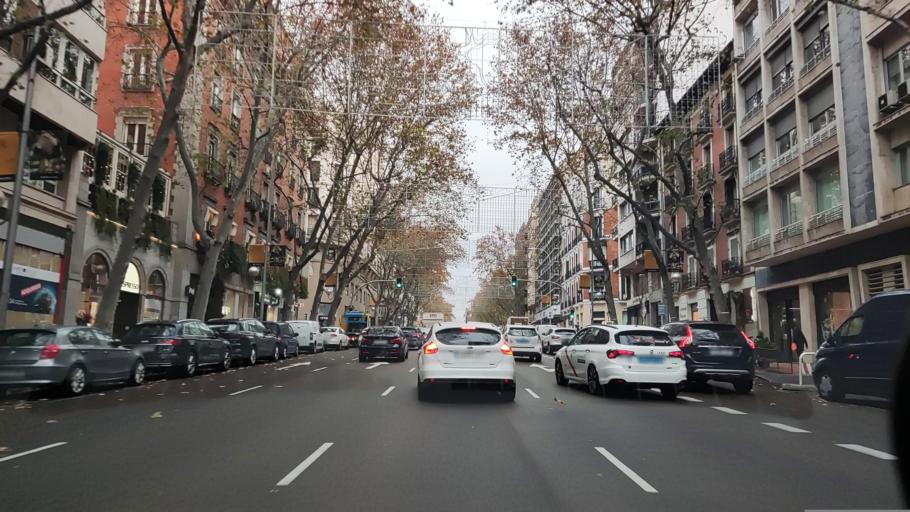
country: ES
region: Madrid
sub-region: Provincia de Madrid
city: Salamanca
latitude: 40.4256
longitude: -3.6841
